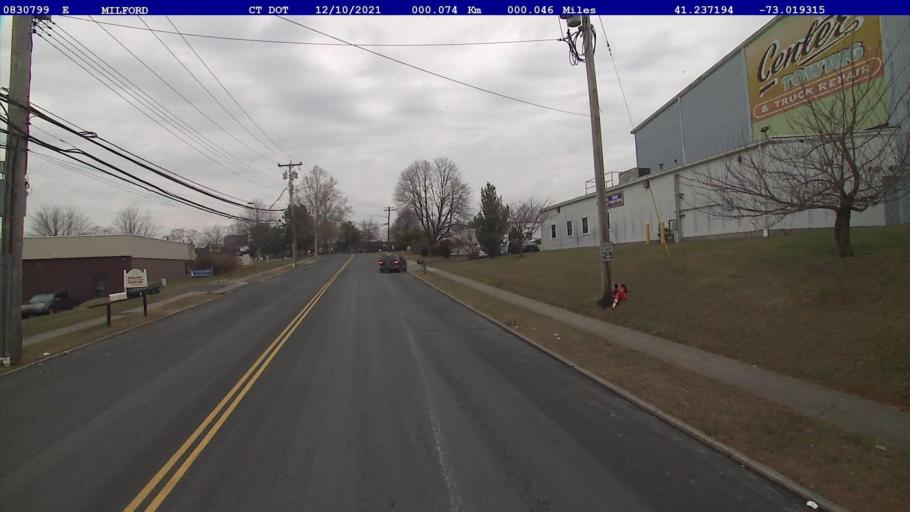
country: US
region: Connecticut
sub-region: New Haven County
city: Woodmont
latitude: 41.2372
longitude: -73.0194
